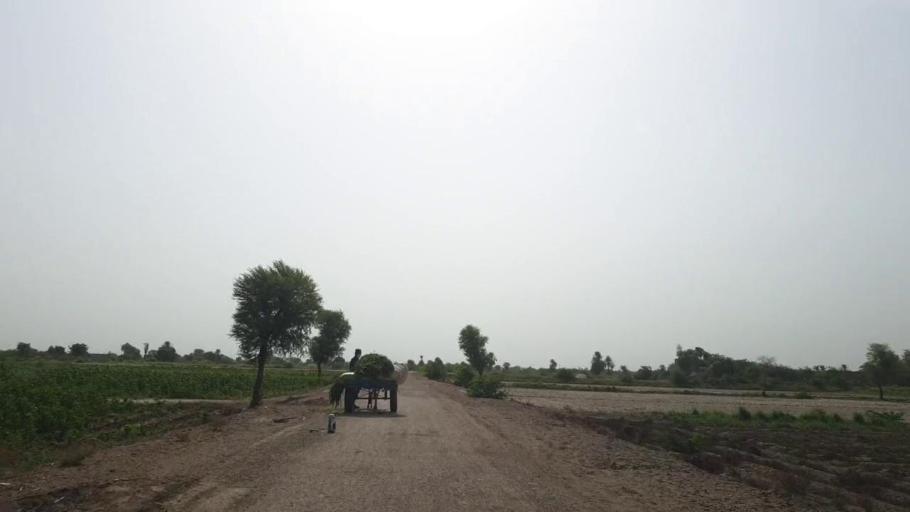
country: PK
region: Sindh
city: Nawabshah
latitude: 26.1146
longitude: 68.4384
